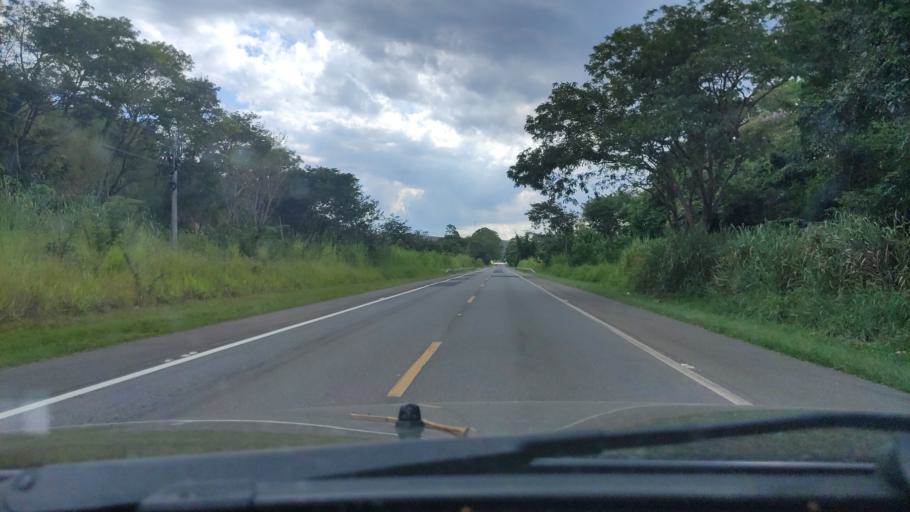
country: BR
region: Sao Paulo
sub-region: Itapira
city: Itapira
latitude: -22.4600
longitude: -46.7300
